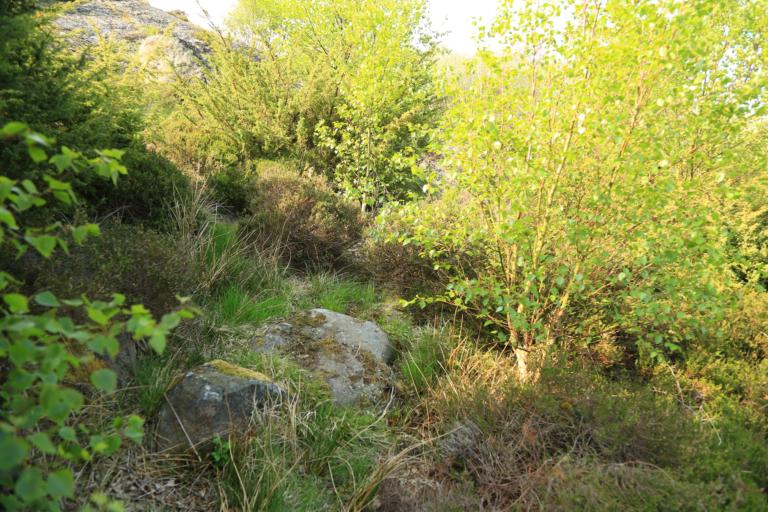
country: SE
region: Halland
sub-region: Varbergs Kommun
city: Varberg
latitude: 57.1583
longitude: 12.2387
